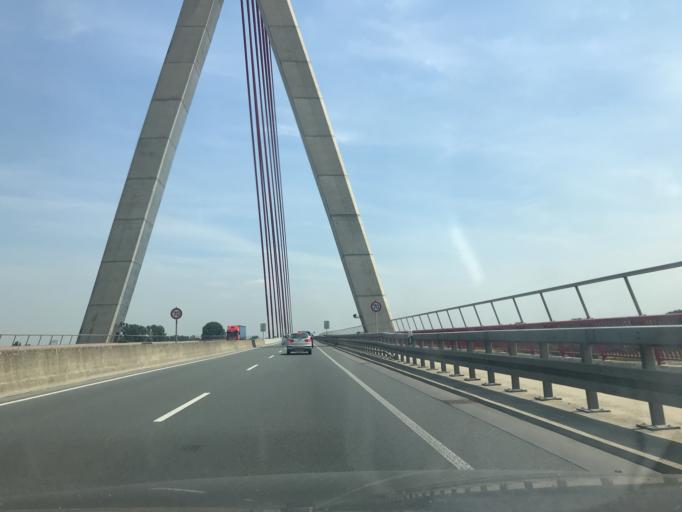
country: DE
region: North Rhine-Westphalia
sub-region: Regierungsbezirk Dusseldorf
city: Wesel
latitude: 51.6450
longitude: 6.6011
